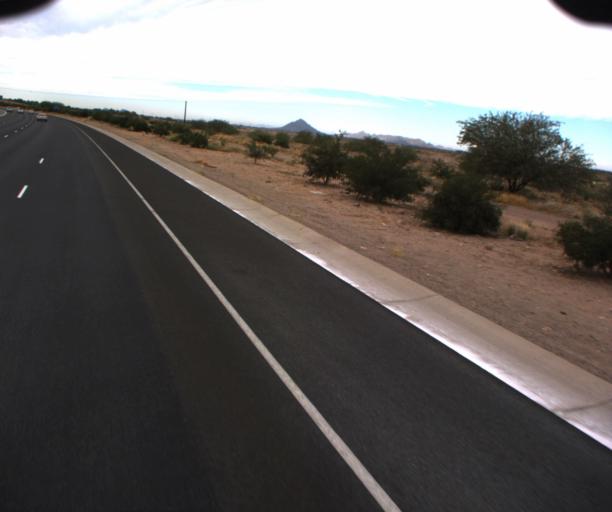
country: US
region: Arizona
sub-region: Maricopa County
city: Mesa
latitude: 33.4829
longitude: -111.7624
